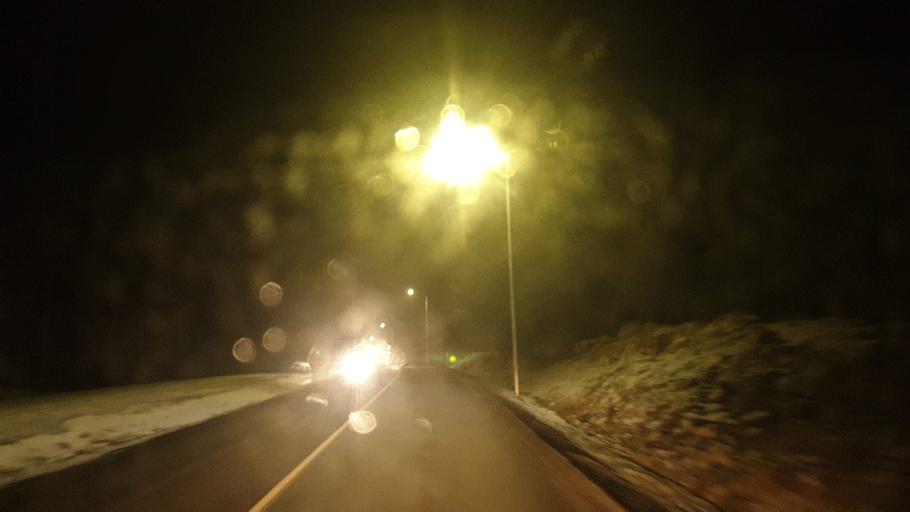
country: FI
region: Southern Savonia
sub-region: Pieksaemaeki
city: Juva
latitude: 61.8832
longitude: 27.7850
